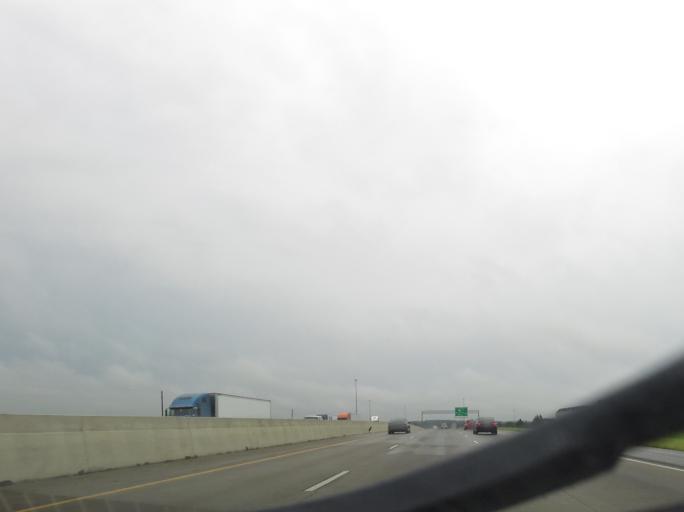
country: US
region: Georgia
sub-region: Crisp County
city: Cordele
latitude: 31.9406
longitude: -83.7486
